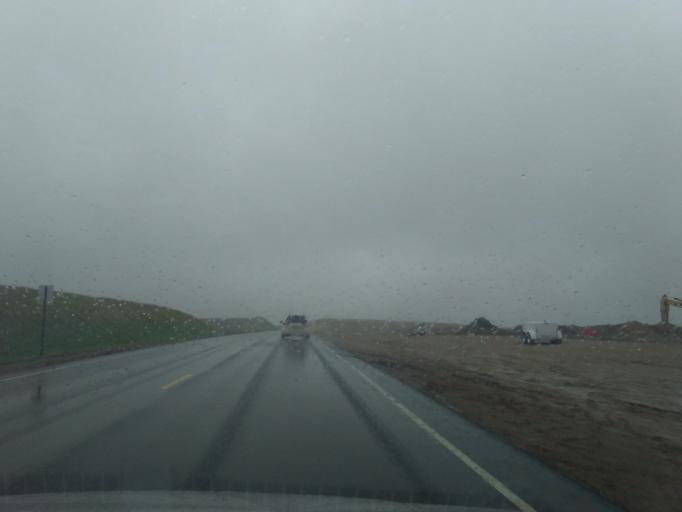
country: US
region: Nebraska
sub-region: Wayne County
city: Wayne
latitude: 42.2155
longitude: -97.1738
